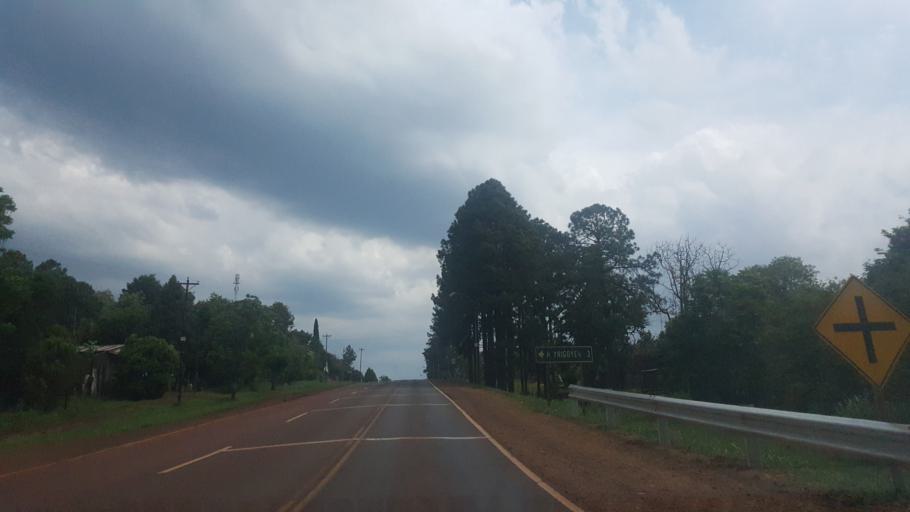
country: AR
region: Misiones
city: Jardin America
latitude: -27.0822
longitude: -55.2851
